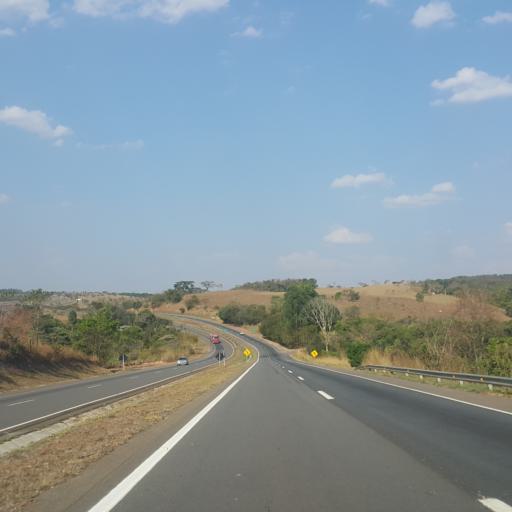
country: BR
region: Goias
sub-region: Abadiania
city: Abadiania
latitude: -16.1148
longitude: -48.5551
